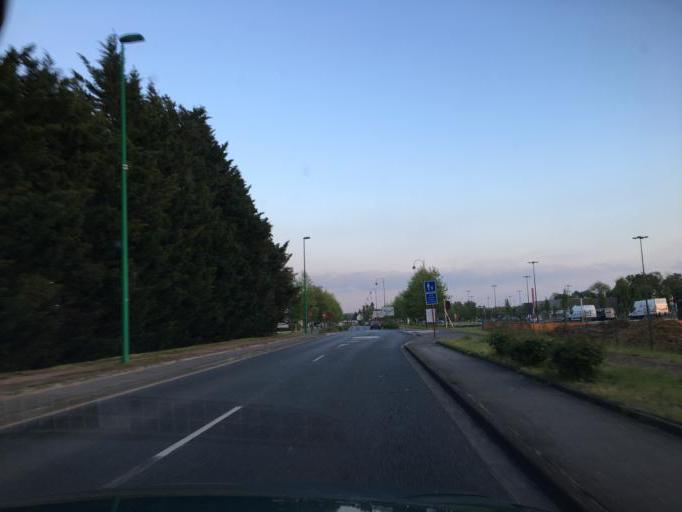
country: FR
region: Centre
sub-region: Departement du Loiret
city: Saint-Pryve-Saint-Mesmin
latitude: 47.8841
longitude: 1.8640
